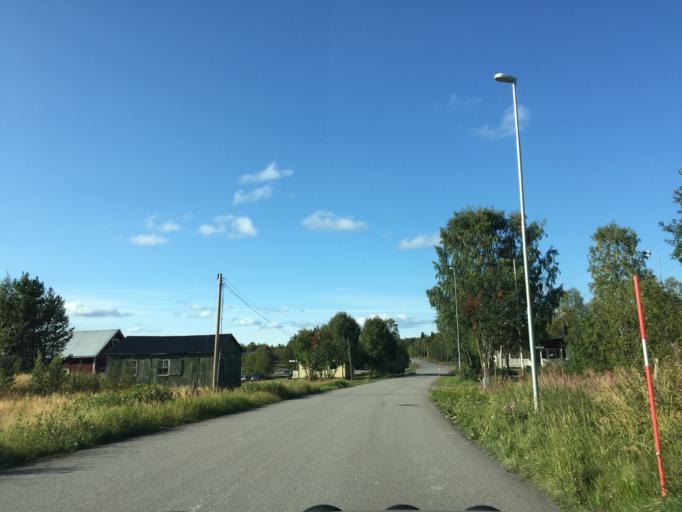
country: SE
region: Norrbotten
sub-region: Gallivare Kommun
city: Malmberget
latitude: 67.6467
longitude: 21.0490
